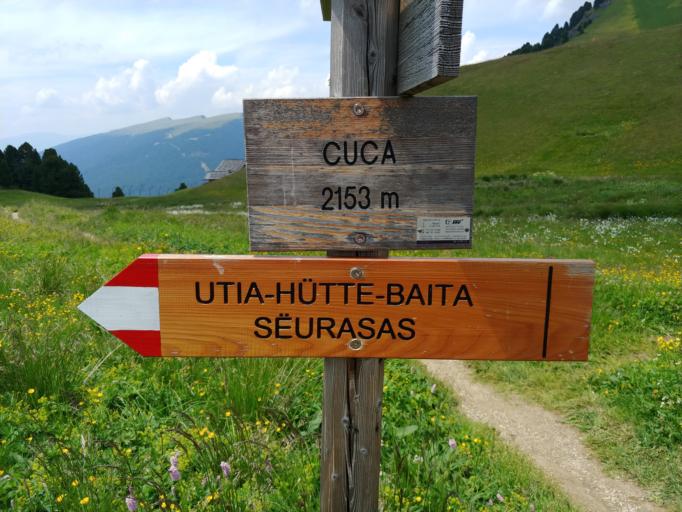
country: IT
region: Trentino-Alto Adige
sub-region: Bolzano
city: Santa Cristina Valgardena
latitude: 46.5874
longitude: 11.7240
